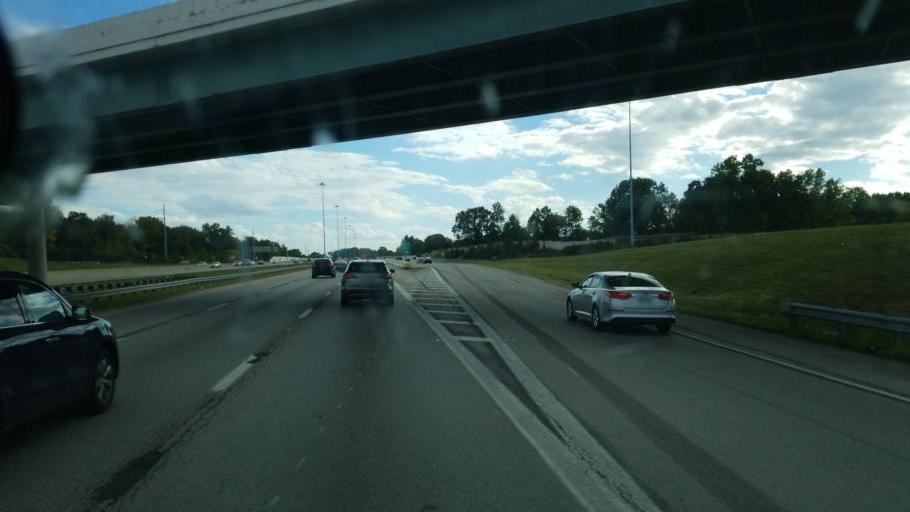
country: US
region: Ohio
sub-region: Franklin County
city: Huber Ridge
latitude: 40.0813
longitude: -82.9074
